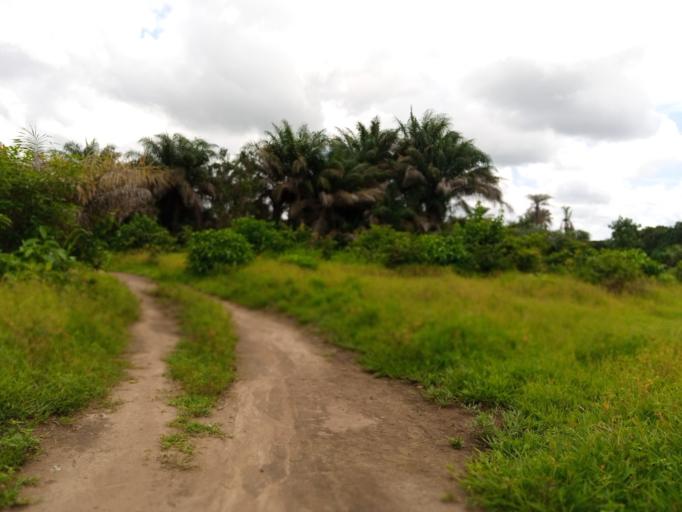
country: SL
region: Northern Province
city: Masoyila
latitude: 8.5887
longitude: -13.1674
